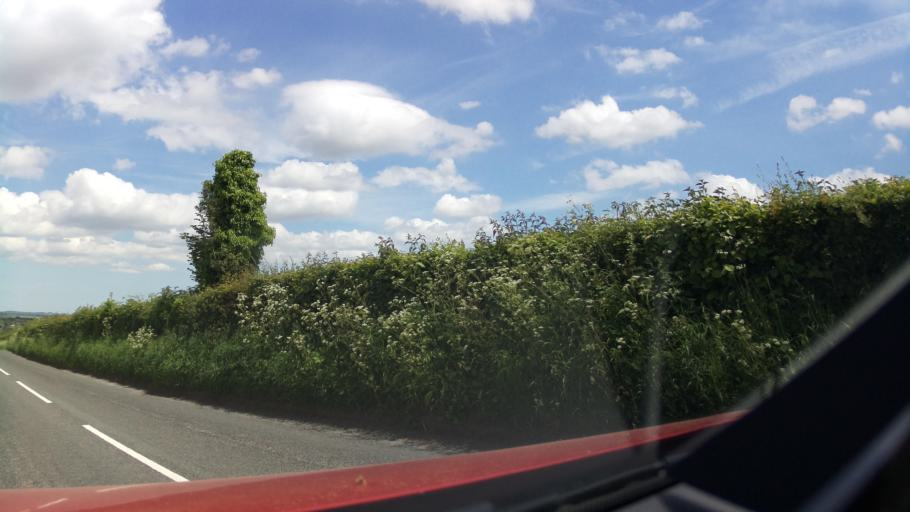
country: GB
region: England
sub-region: Herefordshire
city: Llanrothal
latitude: 51.8927
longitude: -2.7377
